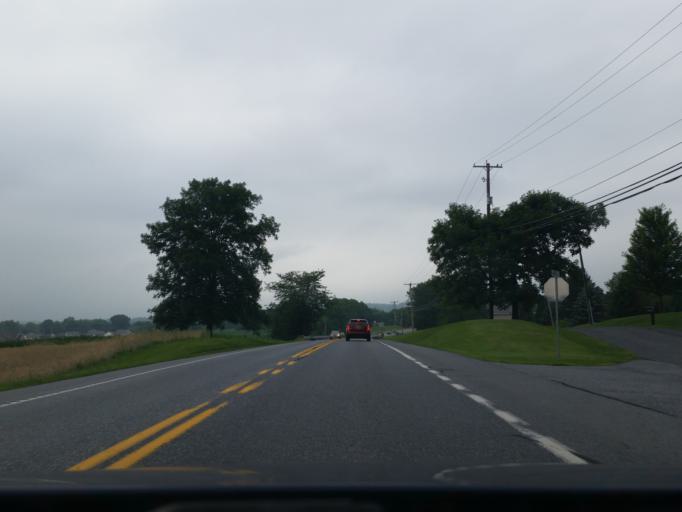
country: US
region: Pennsylvania
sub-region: Lebanon County
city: Annville
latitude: 40.3161
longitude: -76.5064
